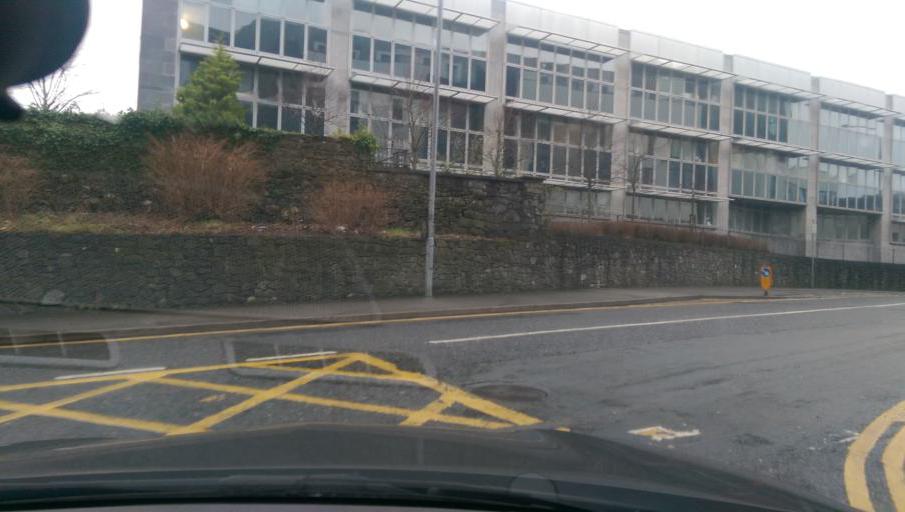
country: IE
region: Connaught
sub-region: County Galway
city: Gaillimh
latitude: 53.2761
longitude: -9.0493
